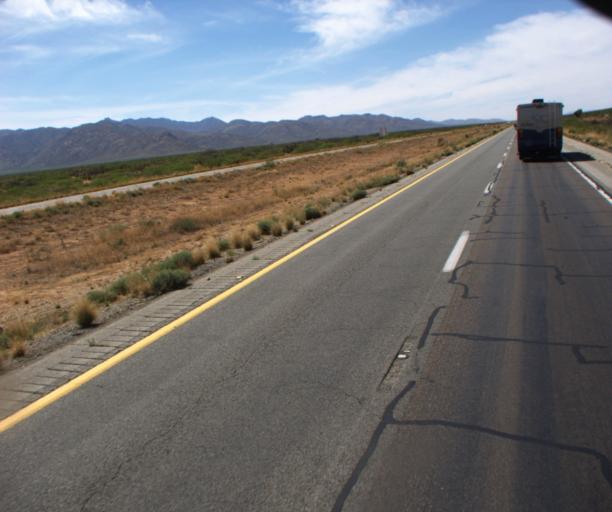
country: US
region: Arizona
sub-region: Cochise County
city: Willcox
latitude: 32.3176
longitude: -109.4644
